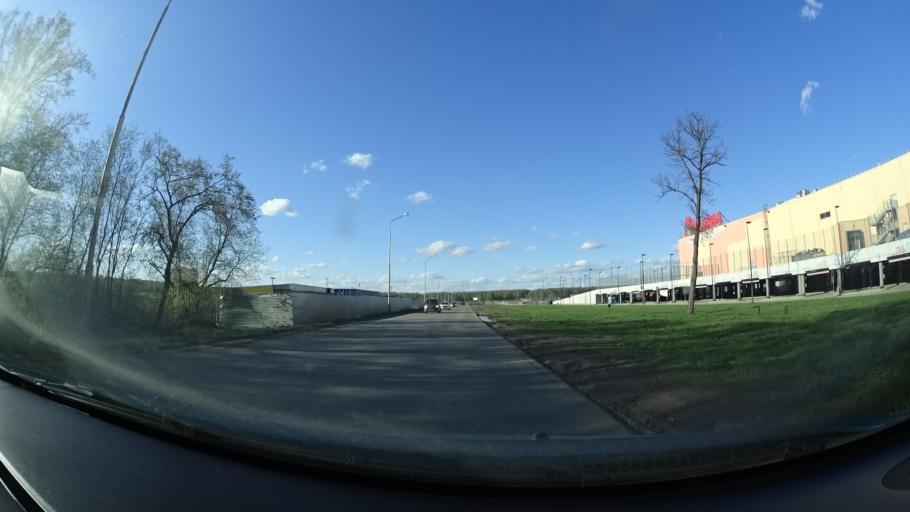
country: RU
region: Bashkortostan
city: Ufa
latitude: 54.6745
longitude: 55.9255
